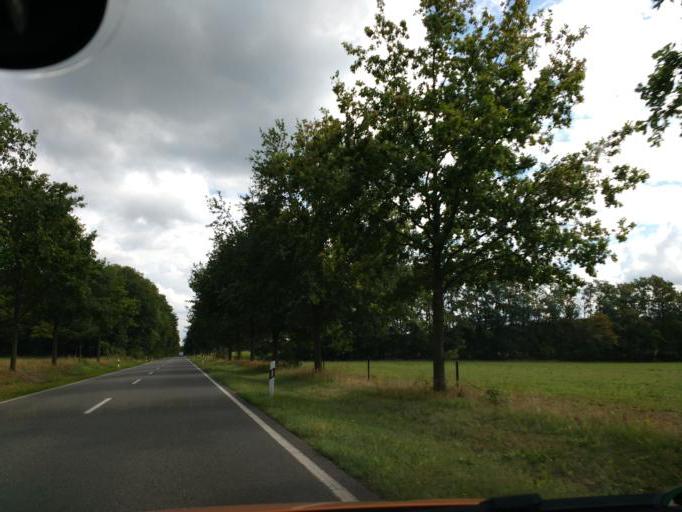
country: DE
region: Brandenburg
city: Marienwerder
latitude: 52.8537
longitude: 13.5680
